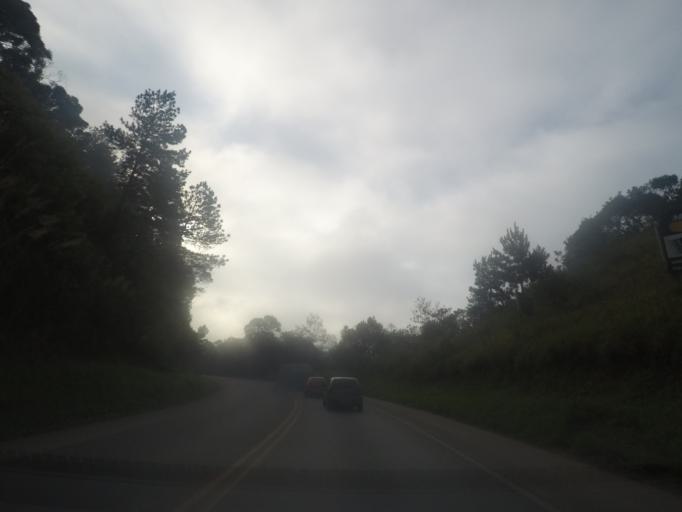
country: BR
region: Parana
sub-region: Almirante Tamandare
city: Almirante Tamandare
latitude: -25.3306
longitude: -49.2918
